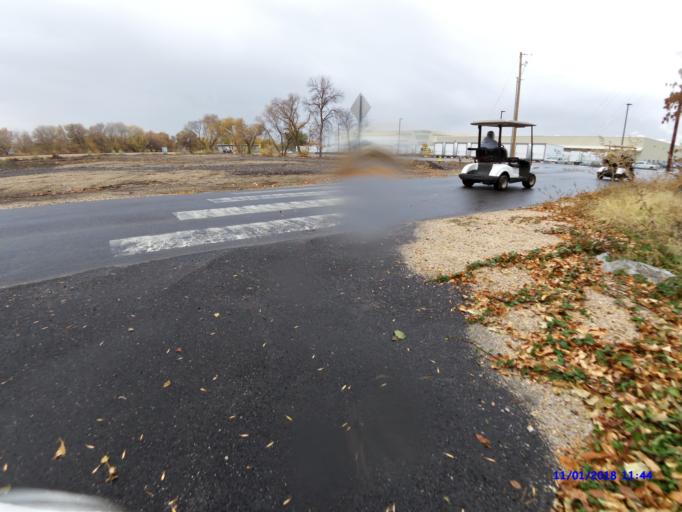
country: US
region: Utah
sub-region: Weber County
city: Ogden
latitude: 41.2363
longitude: -111.9871
